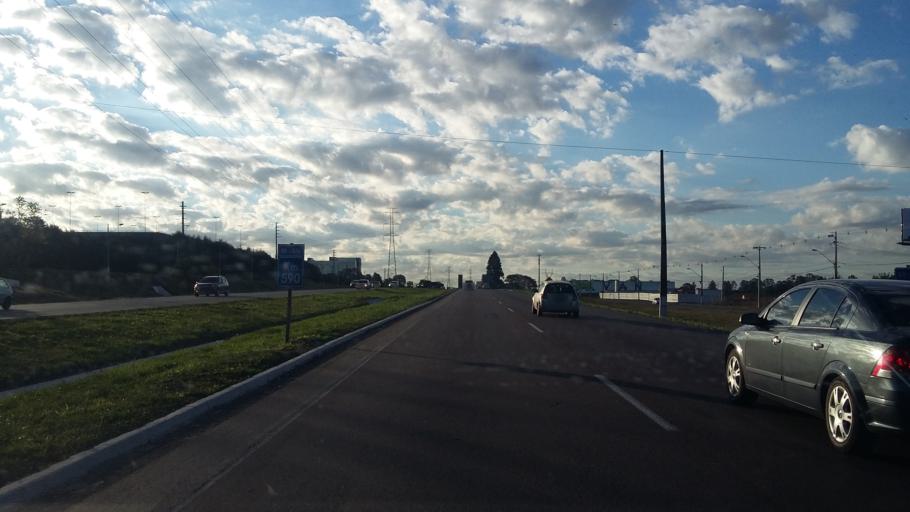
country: BR
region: Parana
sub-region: Curitiba
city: Curitiba
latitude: -25.4589
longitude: -49.3595
